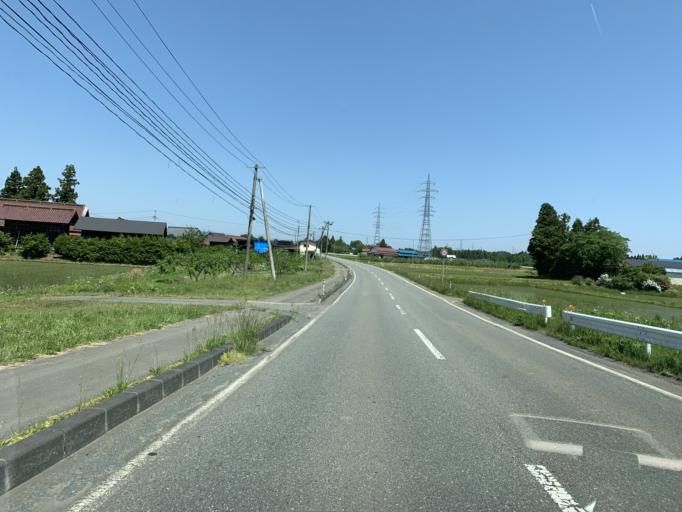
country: JP
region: Iwate
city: Mizusawa
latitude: 39.1760
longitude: 141.0815
